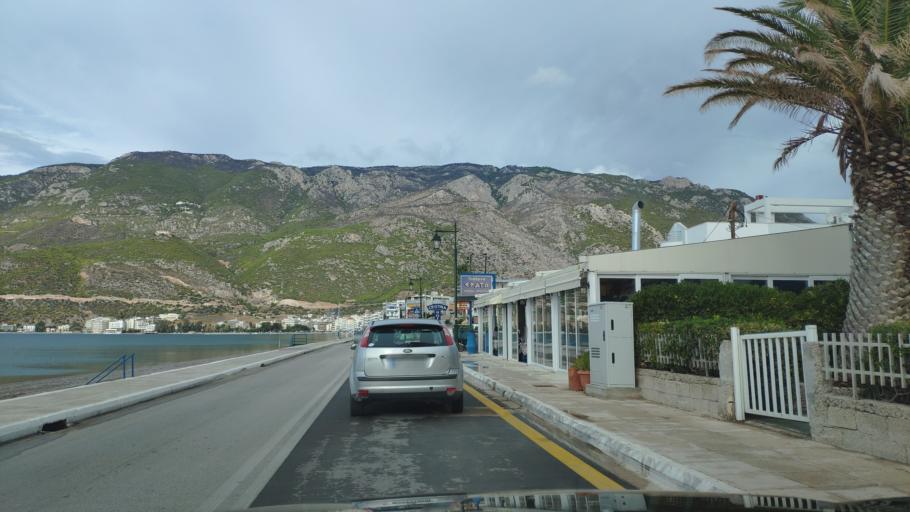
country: GR
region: Peloponnese
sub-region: Nomos Korinthias
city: Loutraki
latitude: 37.9675
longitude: 22.9726
